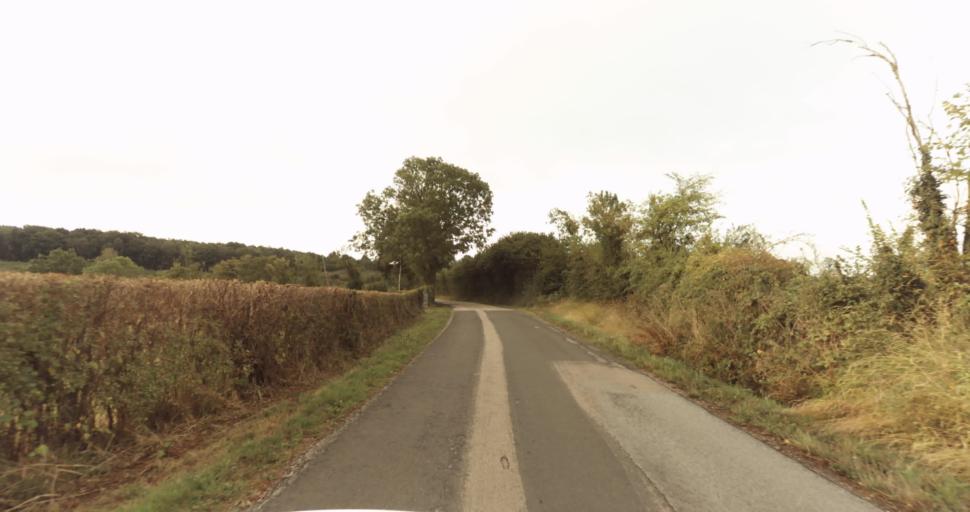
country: FR
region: Lower Normandy
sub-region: Departement de l'Orne
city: Trun
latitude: 48.9071
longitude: 0.1033
